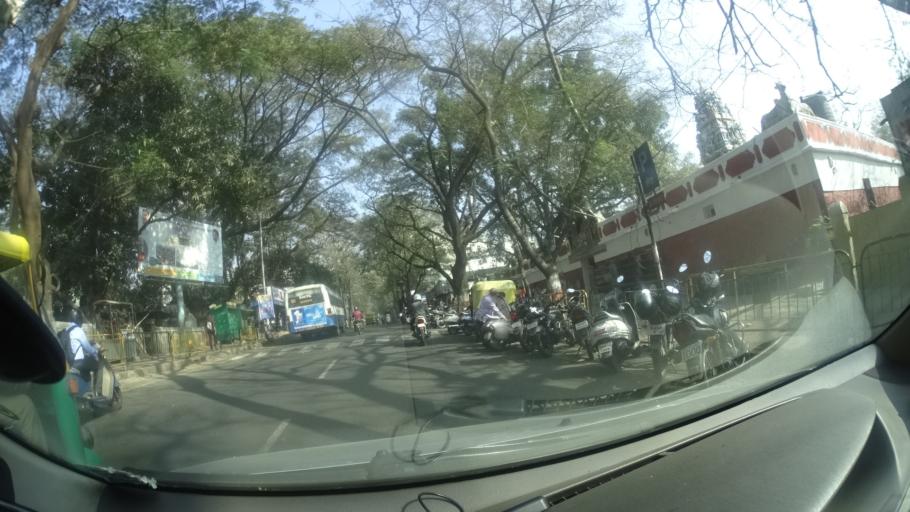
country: IN
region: Karnataka
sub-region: Bangalore Urban
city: Bangalore
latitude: 13.0048
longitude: 77.5713
